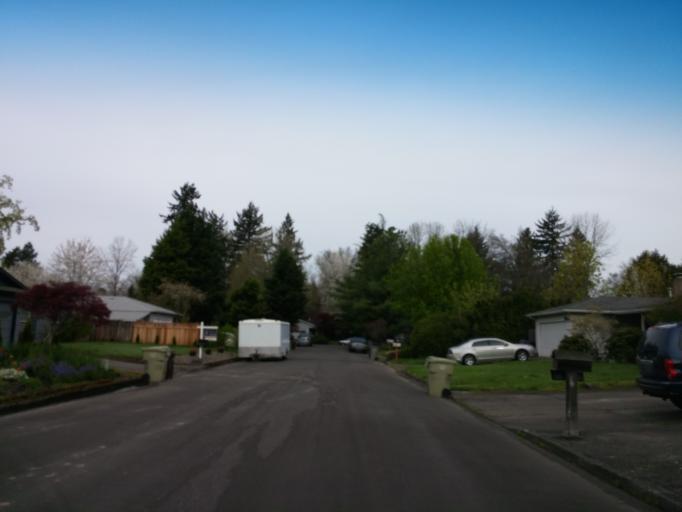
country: US
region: Oregon
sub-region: Washington County
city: Cedar Mill
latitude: 45.5121
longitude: -122.8162
